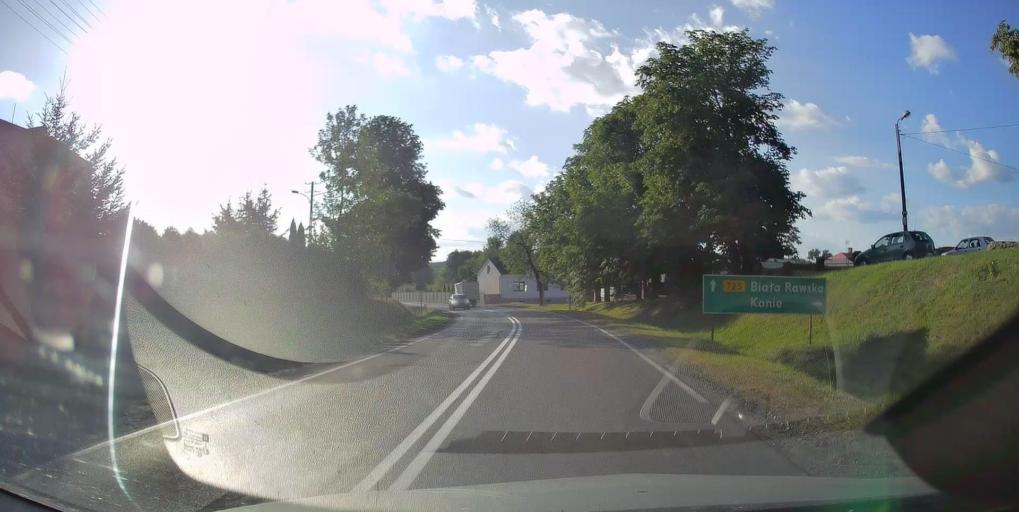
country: PL
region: Masovian Voivodeship
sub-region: Powiat grojecki
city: Bledow
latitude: 51.8000
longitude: 20.6219
